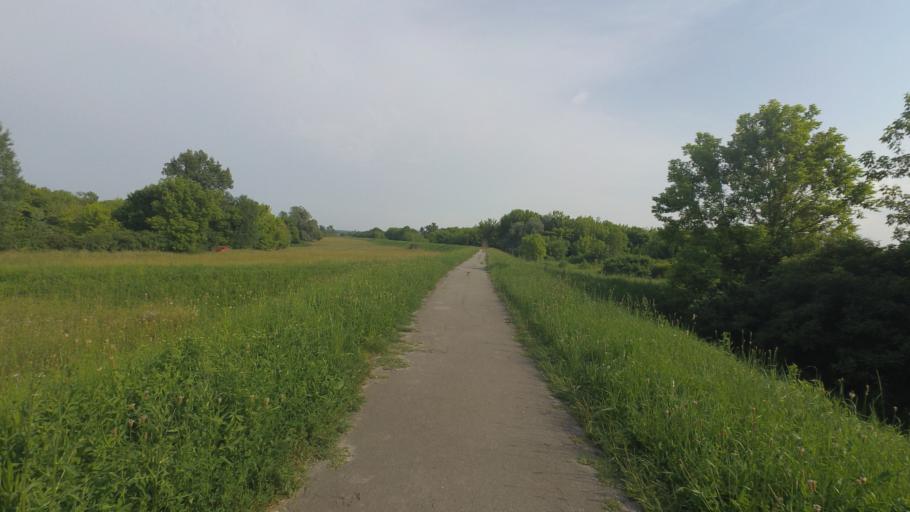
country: HR
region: Karlovacka
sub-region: Grad Karlovac
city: Karlovac
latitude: 45.4995
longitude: 15.5665
